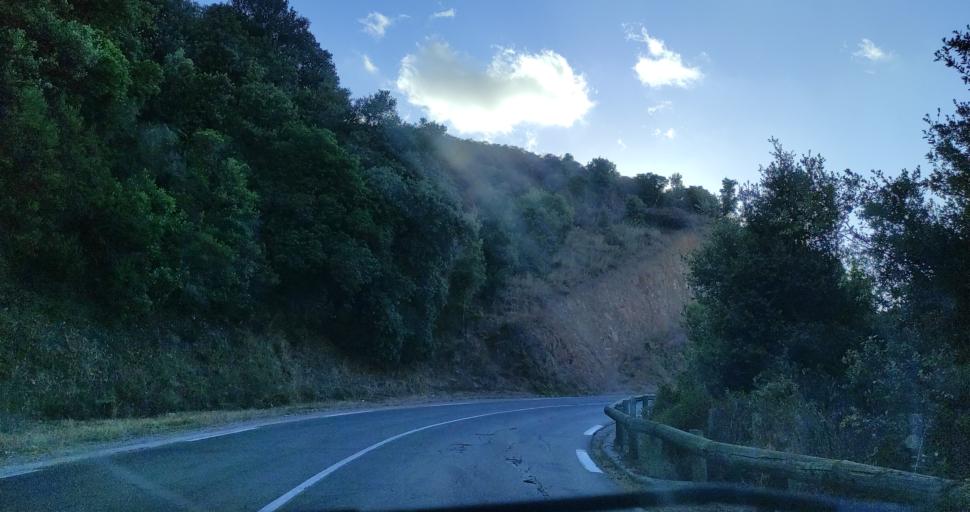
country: FR
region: Corsica
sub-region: Departement de la Corse-du-Sud
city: Appietto
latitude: 42.0216
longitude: 8.7359
